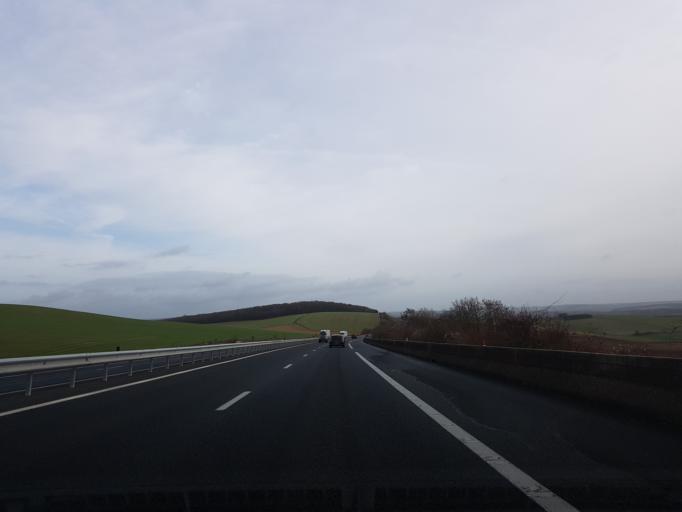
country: FR
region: Bourgogne
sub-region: Departement de l'Yonne
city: Thorigny-sur-Oreuse
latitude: 48.2400
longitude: 3.4678
